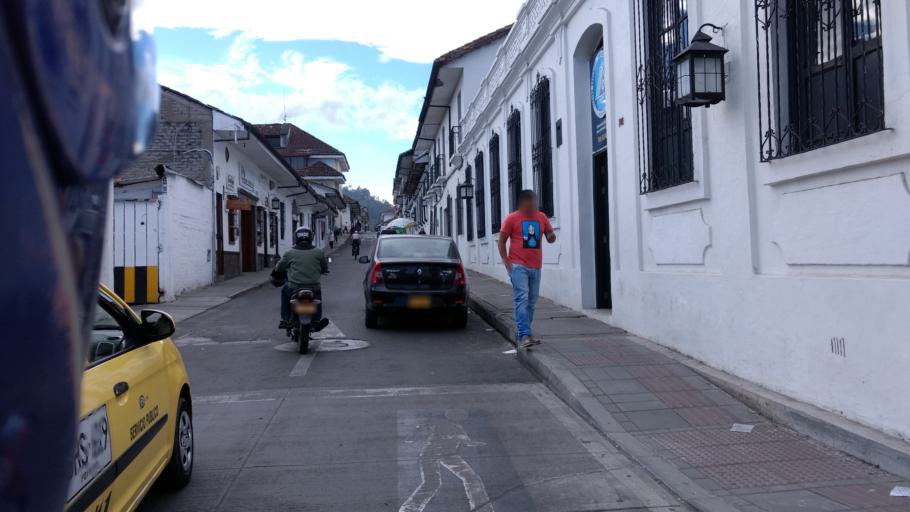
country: CO
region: Cauca
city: Popayan
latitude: 2.4439
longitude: -76.6080
